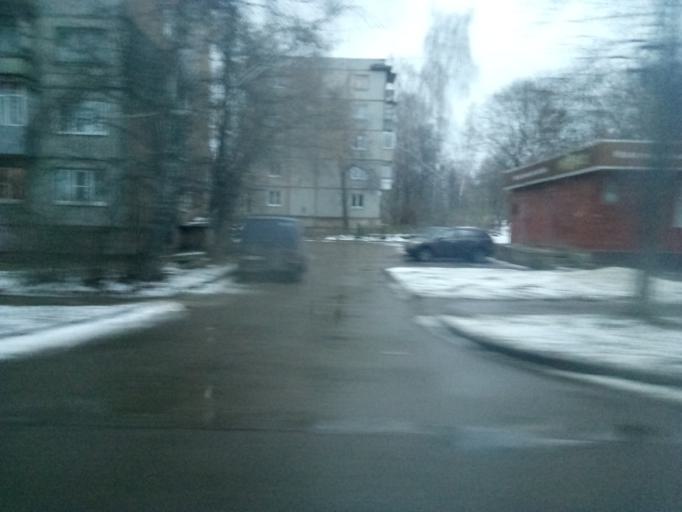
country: RU
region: Tula
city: Kosaya Gora
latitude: 54.1938
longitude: 37.5346
